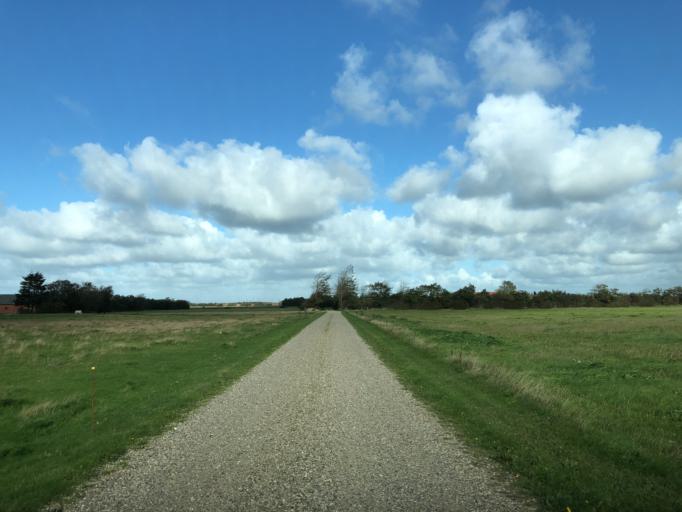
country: DK
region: Central Jutland
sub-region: Holstebro Kommune
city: Ulfborg
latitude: 56.2919
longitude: 8.3215
